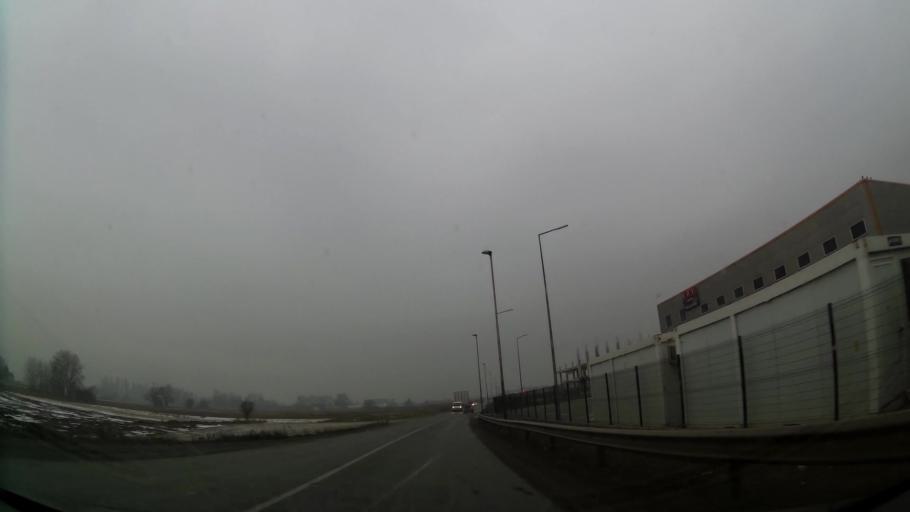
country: MK
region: Cucer-Sandevo
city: Chucher - Sandevo
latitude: 42.0562
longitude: 21.3782
